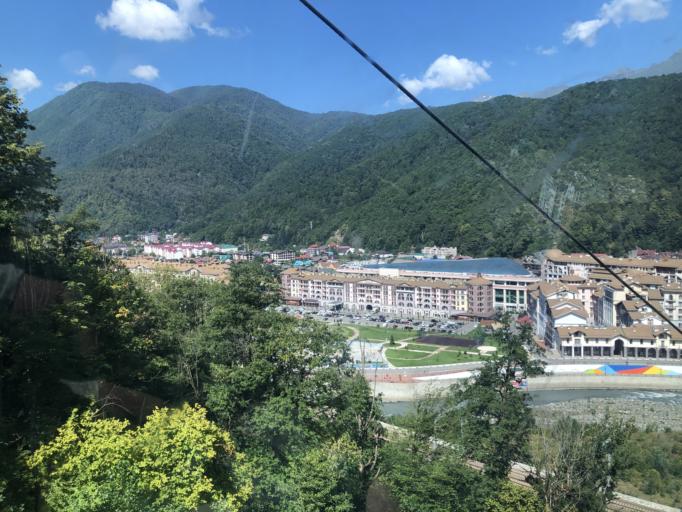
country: RU
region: Krasnodarskiy
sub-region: Sochi City
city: Krasnaya Polyana
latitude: 43.6802
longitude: 40.2653
